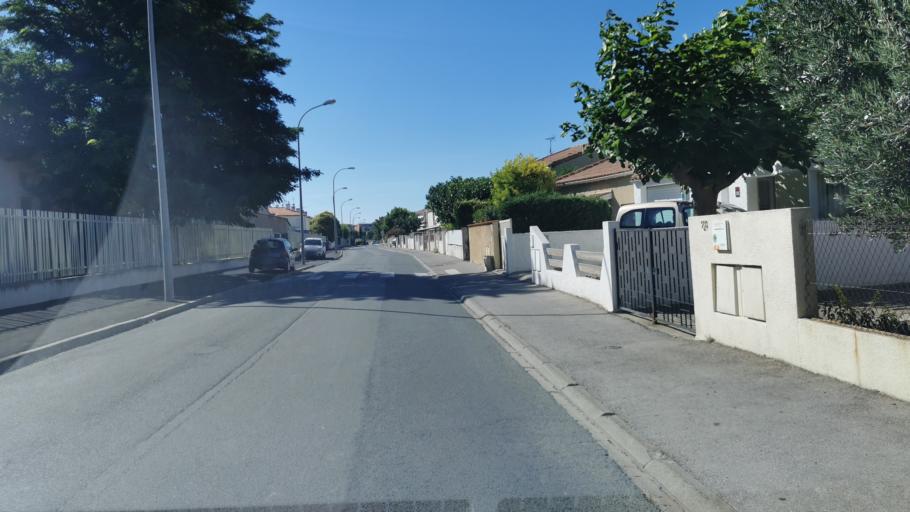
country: FR
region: Languedoc-Roussillon
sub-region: Departement de l'Aude
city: Narbonne
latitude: 43.1915
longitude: 3.0216
